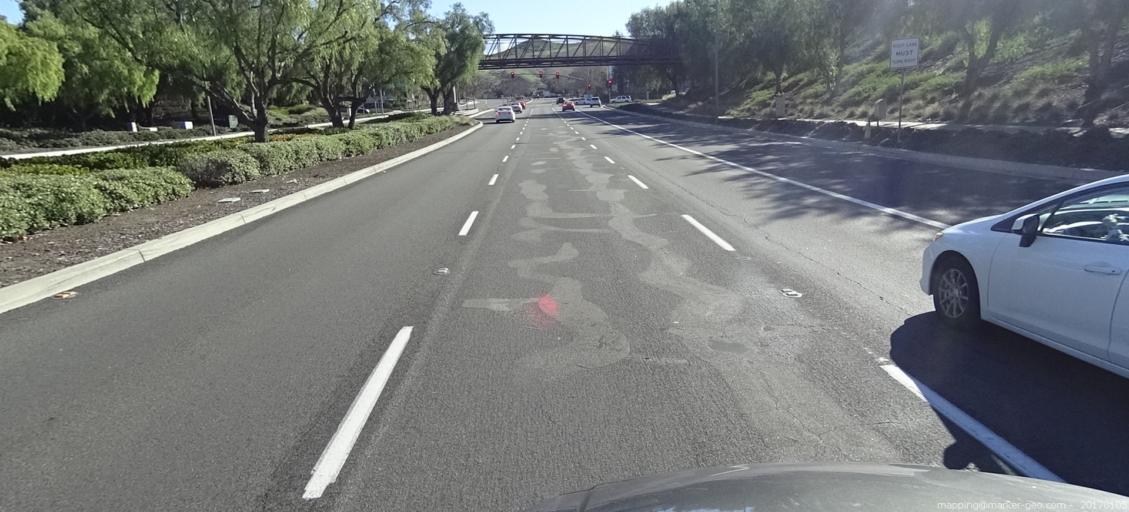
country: US
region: California
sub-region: Orange County
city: Ladera Ranch
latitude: 33.5669
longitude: -117.6336
